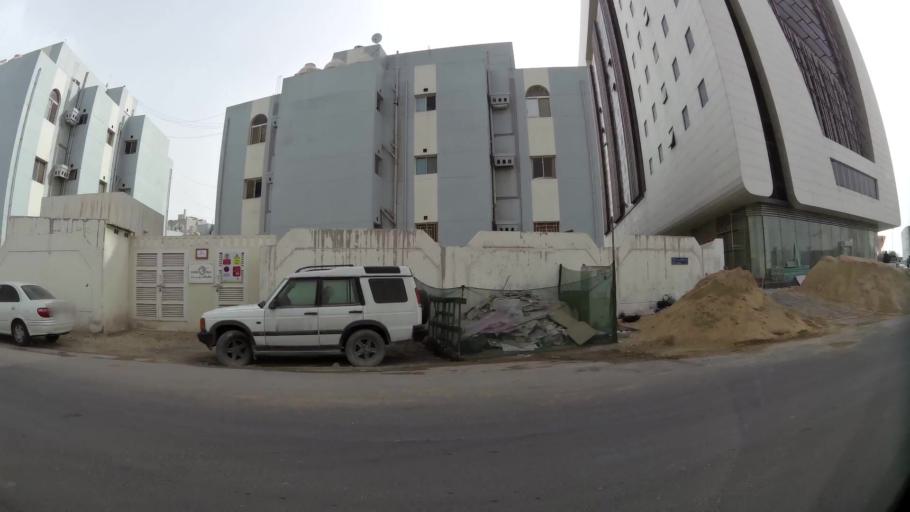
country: QA
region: Baladiyat ad Dawhah
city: Doha
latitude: 25.2746
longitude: 51.5511
